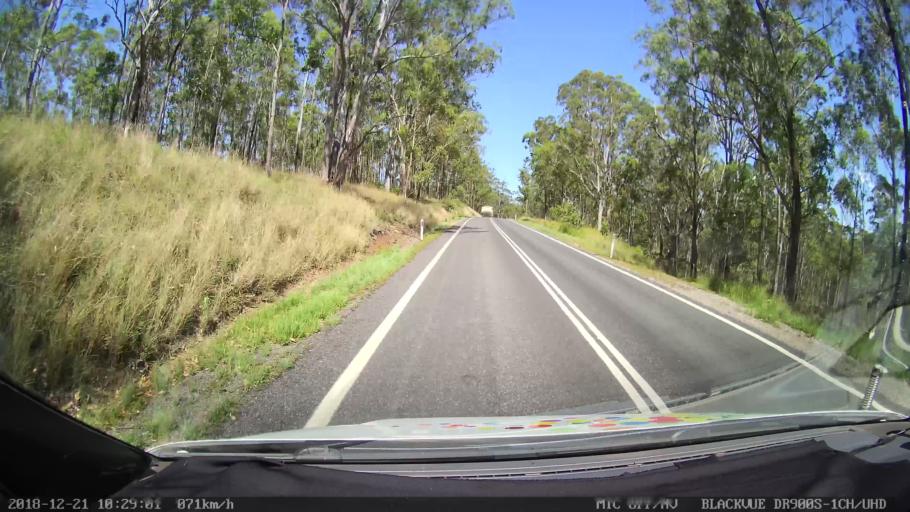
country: AU
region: New South Wales
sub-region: Clarence Valley
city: South Grafton
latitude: -29.6330
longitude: 152.7282
